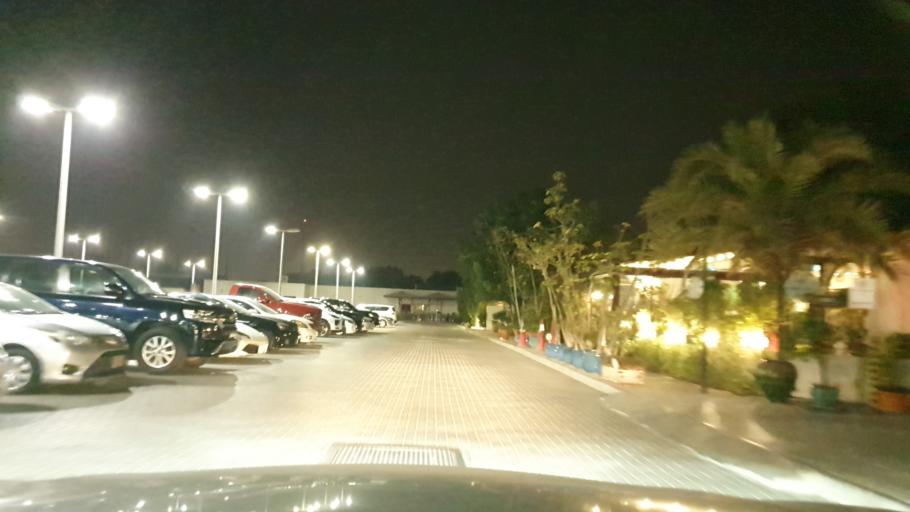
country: BH
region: Manama
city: Jidd Hafs
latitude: 26.1978
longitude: 50.4767
